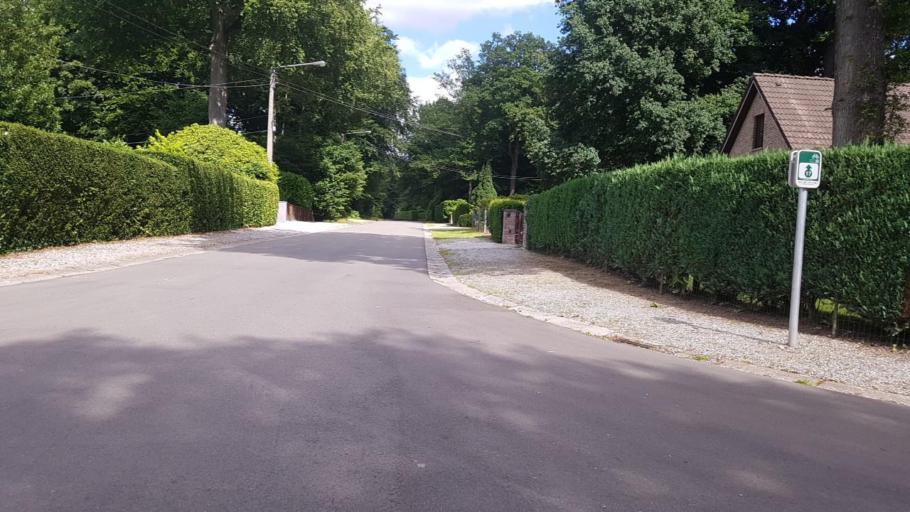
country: BE
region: Wallonia
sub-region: Province du Hainaut
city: Charleroi
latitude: 50.3544
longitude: 4.4362
